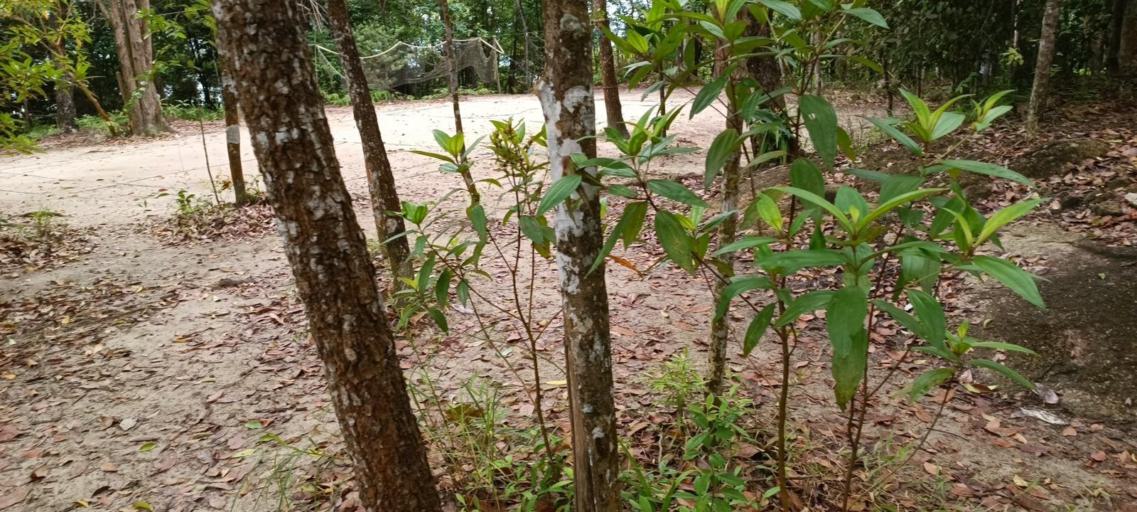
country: MY
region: Penang
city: George Town
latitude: 5.3887
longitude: 100.2909
